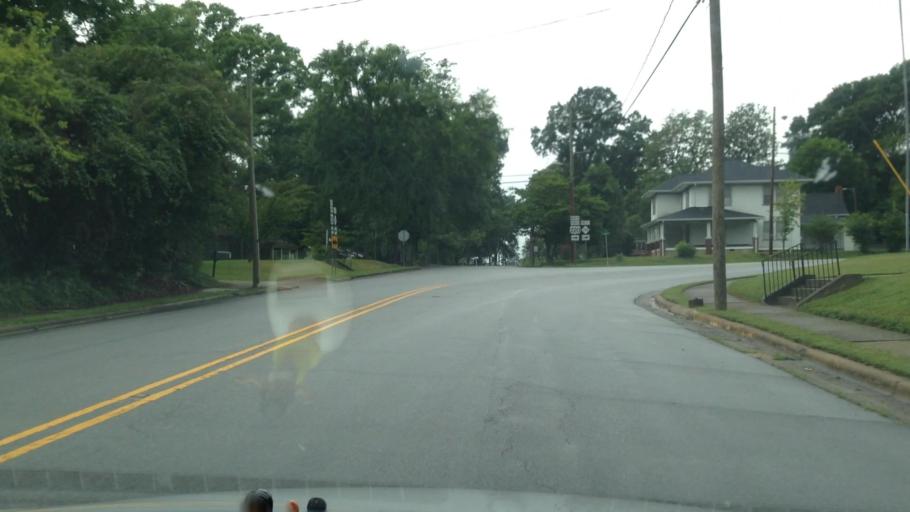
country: US
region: North Carolina
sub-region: Rockingham County
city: Madison
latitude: 36.3886
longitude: -79.9669
